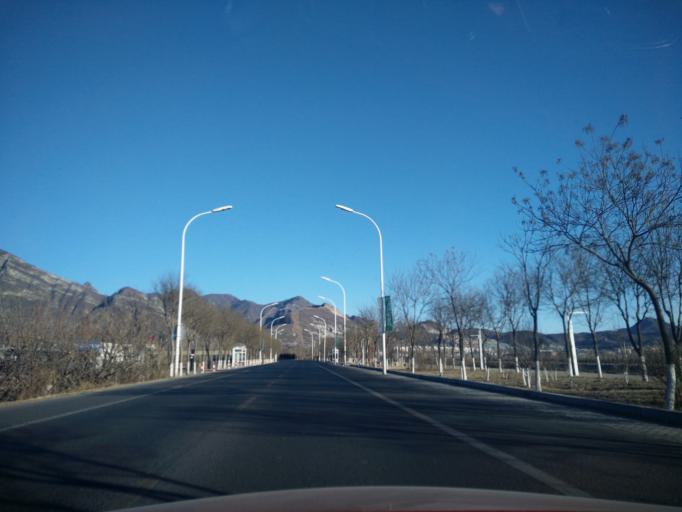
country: CN
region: Beijing
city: Junzhuang
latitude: 39.9876
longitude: 116.0807
